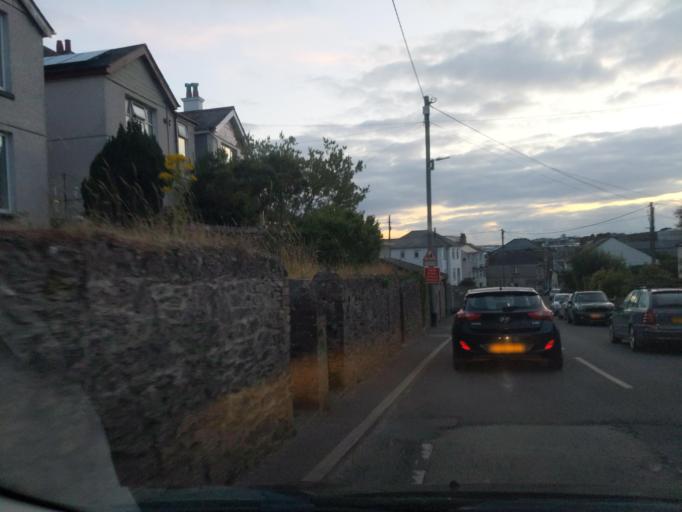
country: GB
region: England
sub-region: Plymouth
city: Plymstock
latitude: 50.3604
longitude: -4.1061
